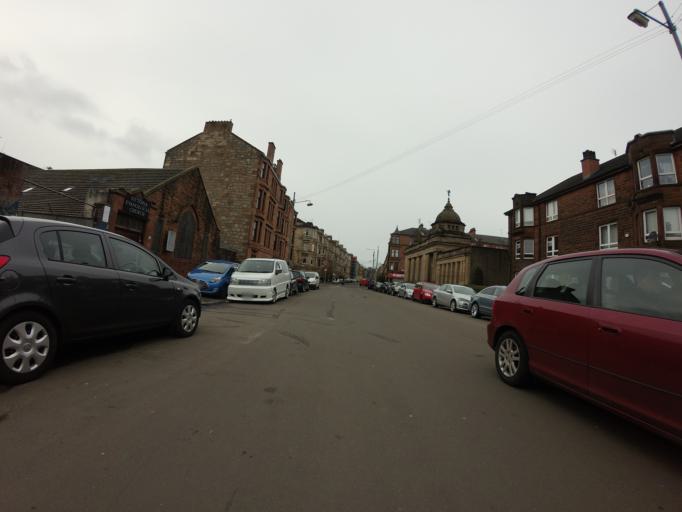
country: GB
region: Scotland
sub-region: Glasgow City
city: Glasgow
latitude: 55.8380
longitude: -4.2611
